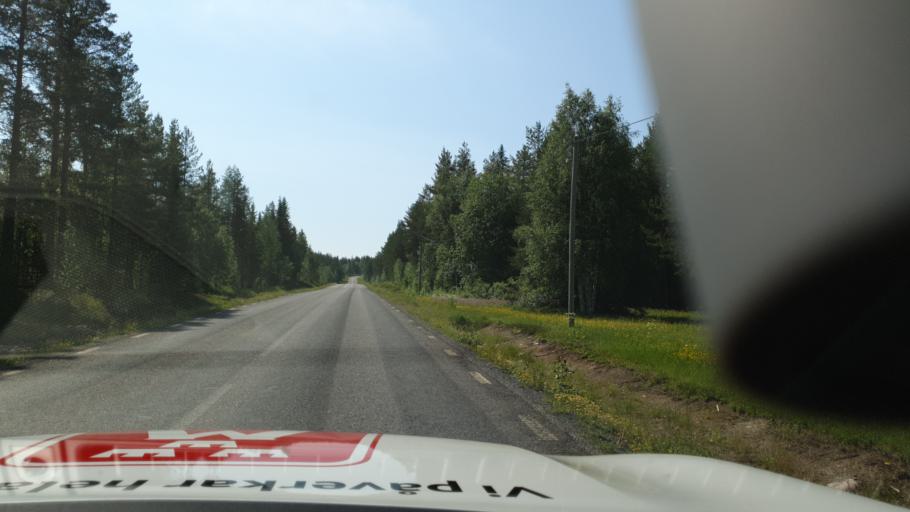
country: SE
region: Vaesterbotten
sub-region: Skelleftea Kommun
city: Langsele
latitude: 64.9995
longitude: 20.0905
